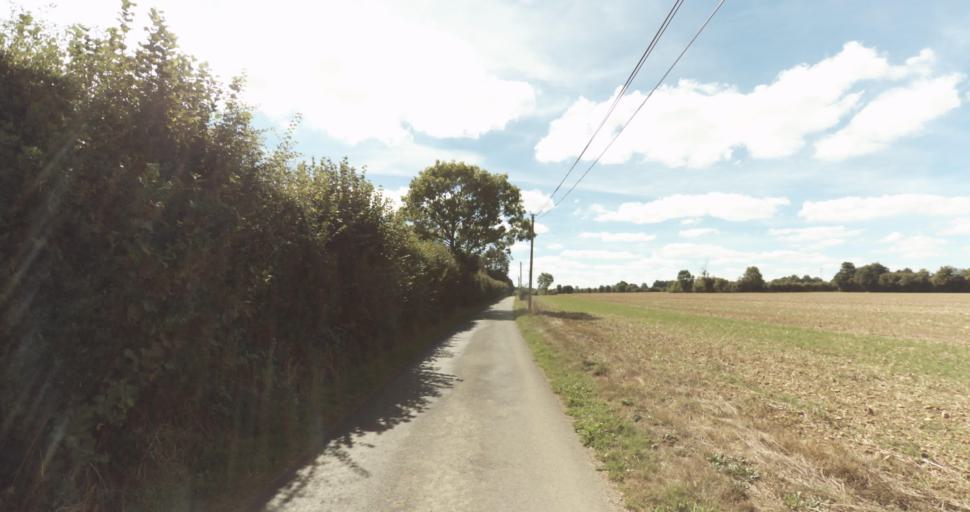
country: FR
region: Lower Normandy
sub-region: Departement de l'Orne
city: Vimoutiers
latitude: 48.9308
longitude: 0.2560
